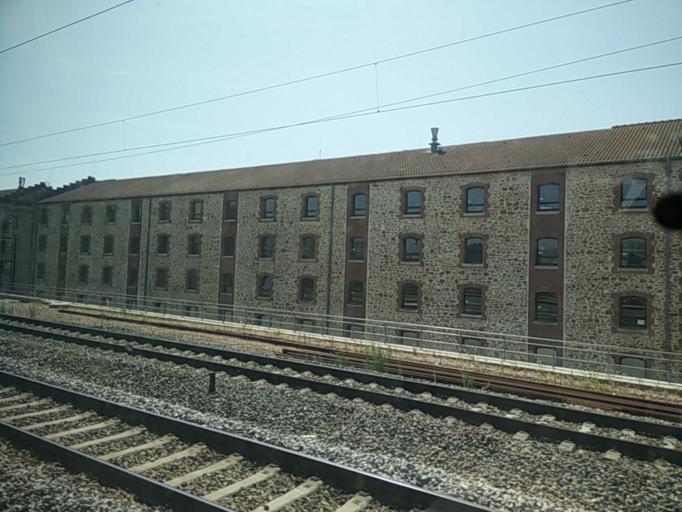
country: FR
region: Ile-de-France
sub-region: Departement de Seine-Saint-Denis
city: Aubervilliers
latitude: 48.8977
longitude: 2.3807
